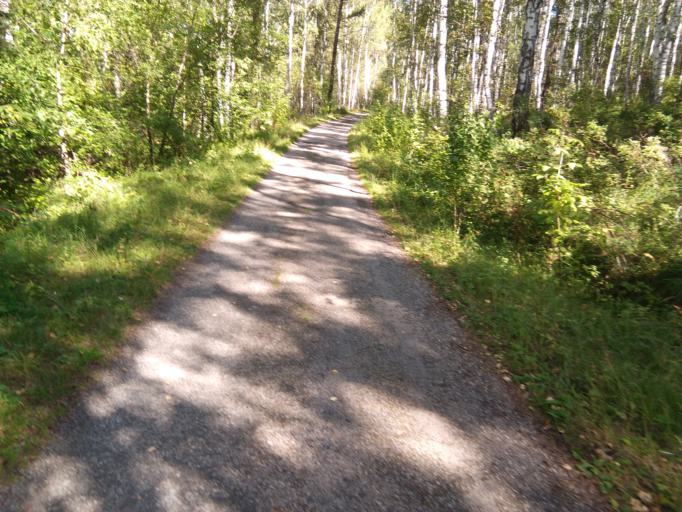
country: RU
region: Bashkortostan
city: Abzakovo
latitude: 53.8146
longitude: 58.6041
